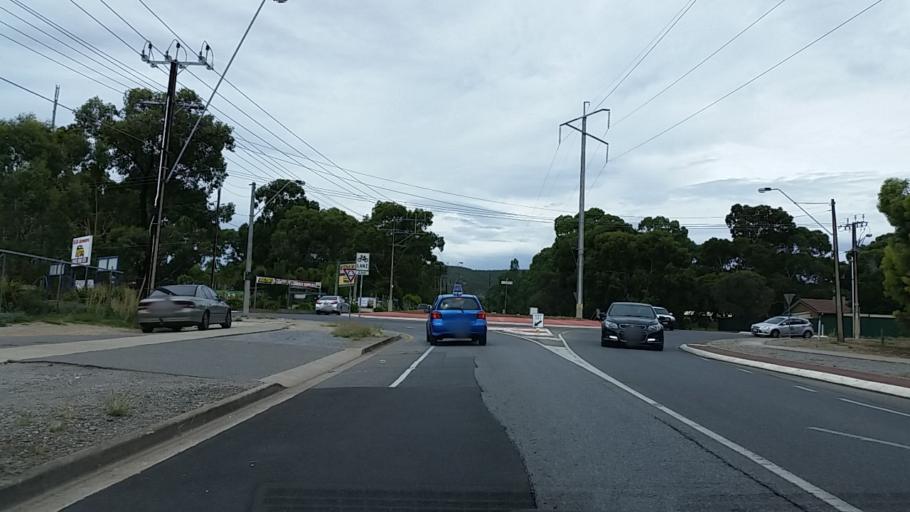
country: AU
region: South Australia
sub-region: Tea Tree Gully
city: Hope Valley
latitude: -34.8324
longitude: 138.7064
